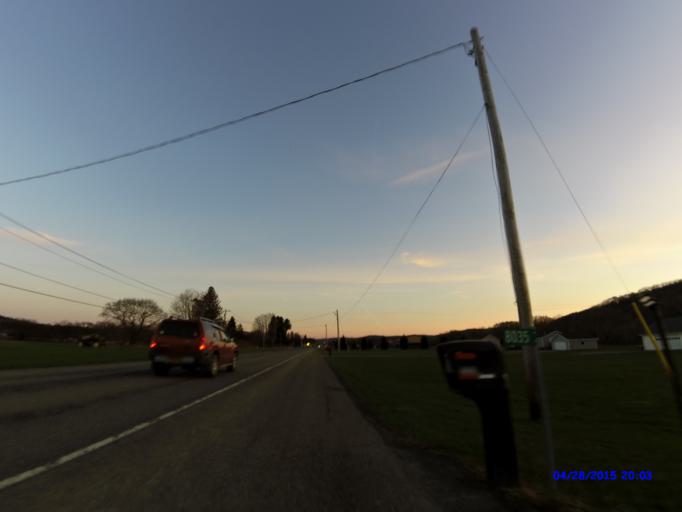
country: US
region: New York
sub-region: Cattaraugus County
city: Franklinville
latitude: 42.3520
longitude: -78.4528
